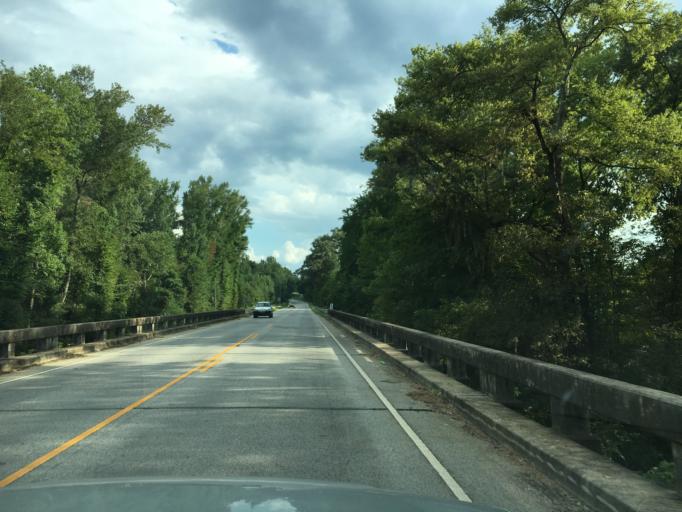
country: US
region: South Carolina
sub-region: Greenwood County
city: Ninety Six
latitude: 34.1953
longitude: -82.0291
